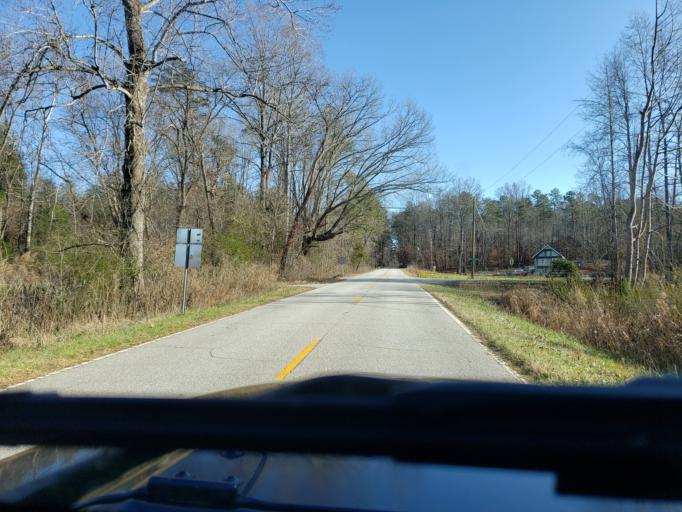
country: US
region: North Carolina
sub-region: Cleveland County
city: White Plains
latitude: 35.1539
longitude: -81.3971
